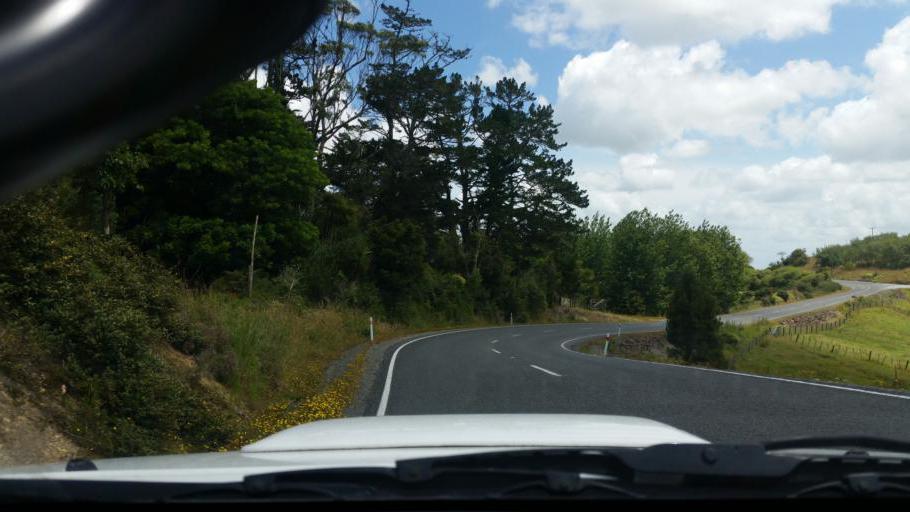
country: NZ
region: Northland
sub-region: Whangarei
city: Ruakaka
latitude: -36.0777
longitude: 174.2437
